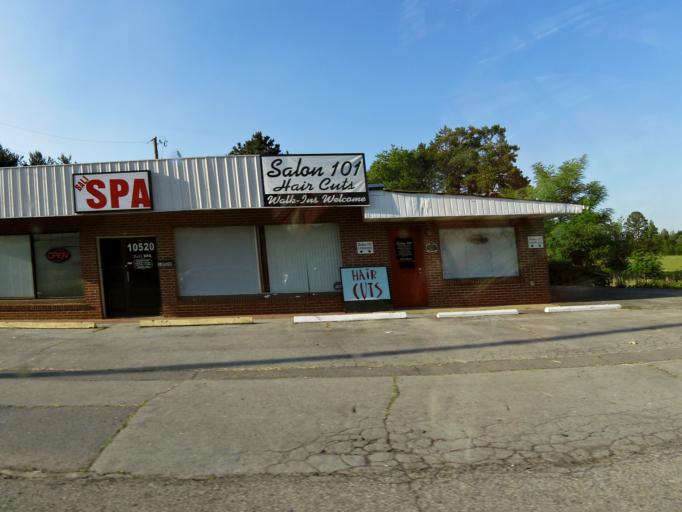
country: US
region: Tennessee
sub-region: Sevier County
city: Seymour
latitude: 35.8807
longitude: -83.7807
